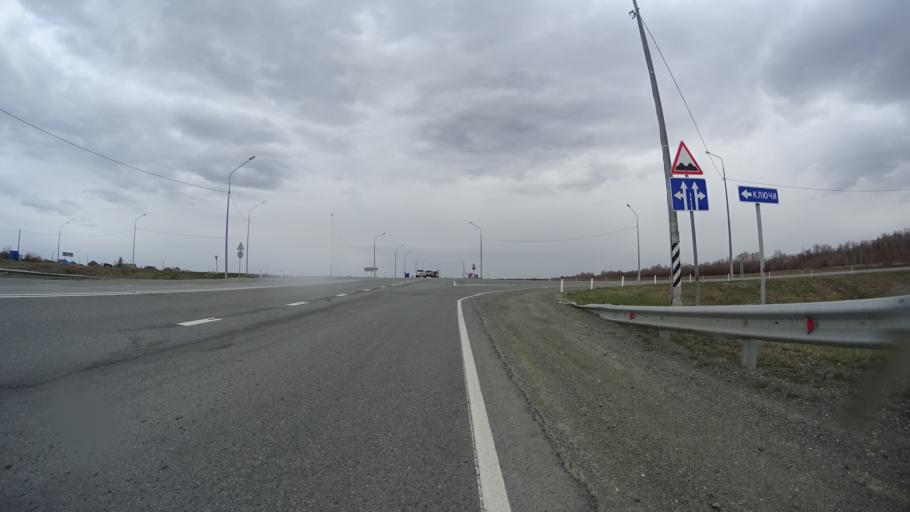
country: RU
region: Chelyabinsk
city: Krasnogorskiy
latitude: 54.6741
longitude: 61.2490
